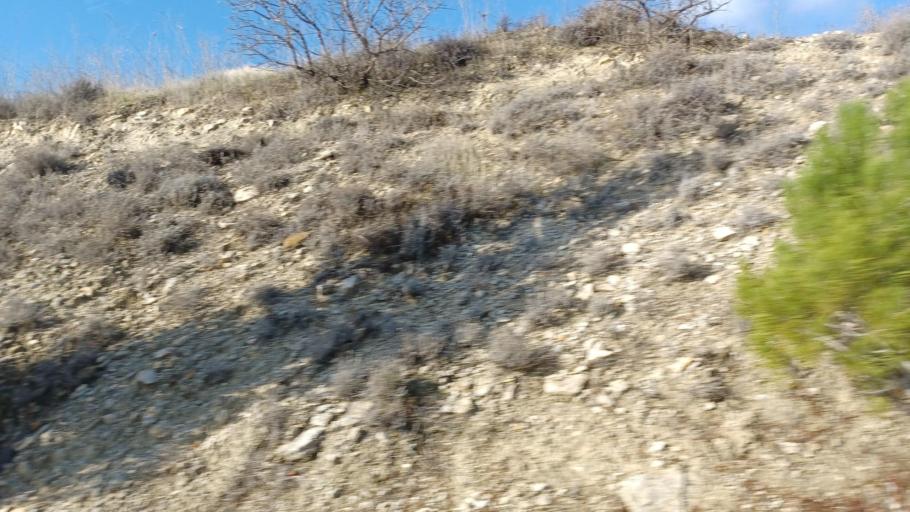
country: CY
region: Limassol
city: Pachna
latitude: 34.8599
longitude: 32.7246
